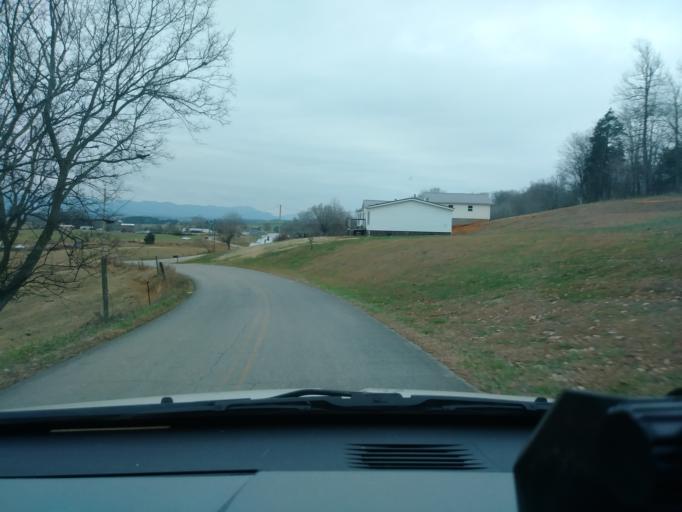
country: US
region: Tennessee
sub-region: Greene County
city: Greeneville
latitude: 36.0939
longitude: -82.8979
